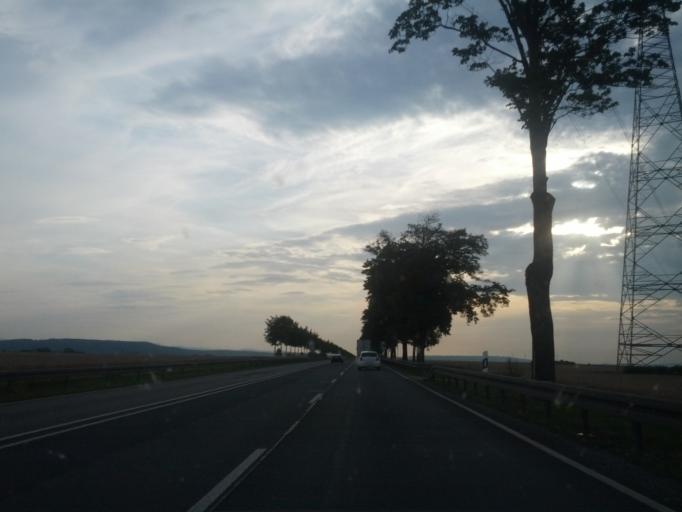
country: DE
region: Thuringia
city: Nottleben
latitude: 50.9473
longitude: 10.8699
